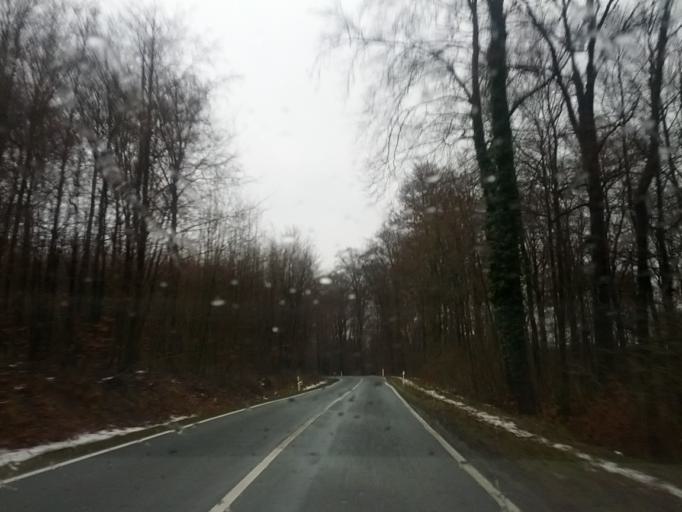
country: DE
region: Thuringia
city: Heyerode
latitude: 51.1675
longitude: 10.3576
